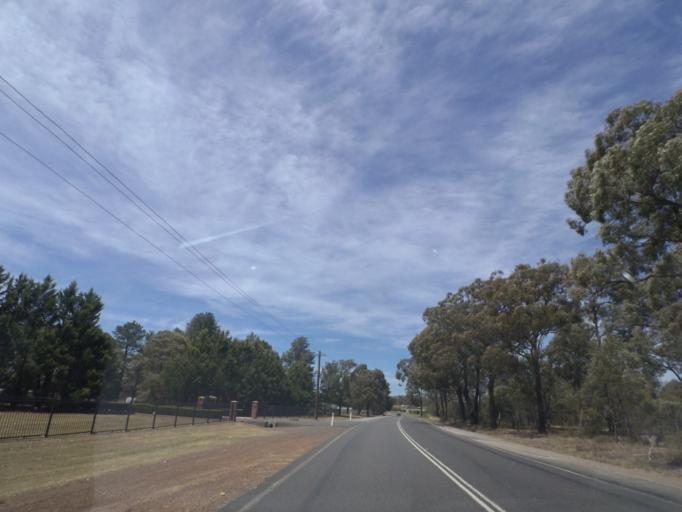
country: AU
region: New South Wales
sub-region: Wollondilly
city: Buxton
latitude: -34.3131
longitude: 150.5867
